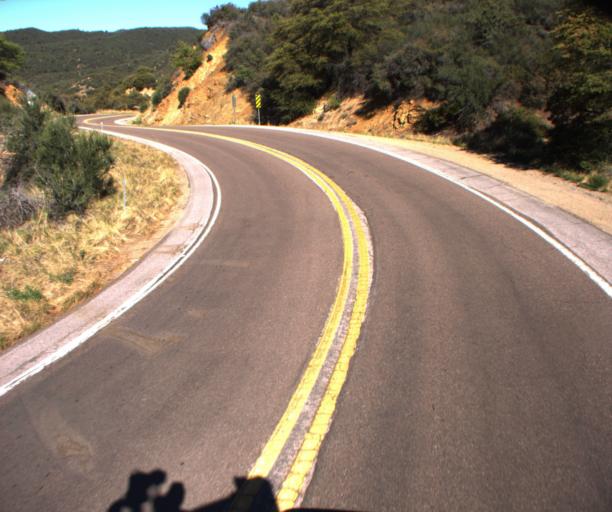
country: US
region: Arizona
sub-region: Yavapai County
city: Prescott
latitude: 34.4540
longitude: -112.5272
